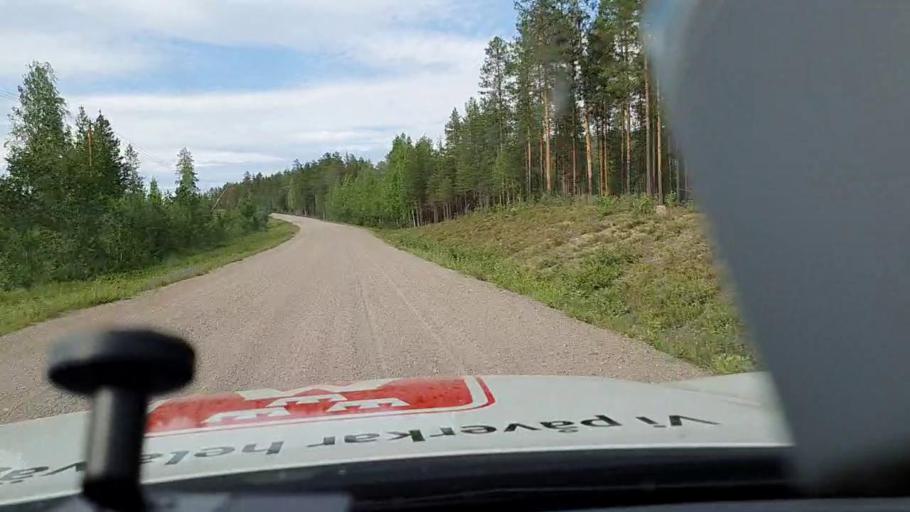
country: SE
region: Norrbotten
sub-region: Alvsbyns Kommun
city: AElvsbyn
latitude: 66.1283
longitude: 20.9978
